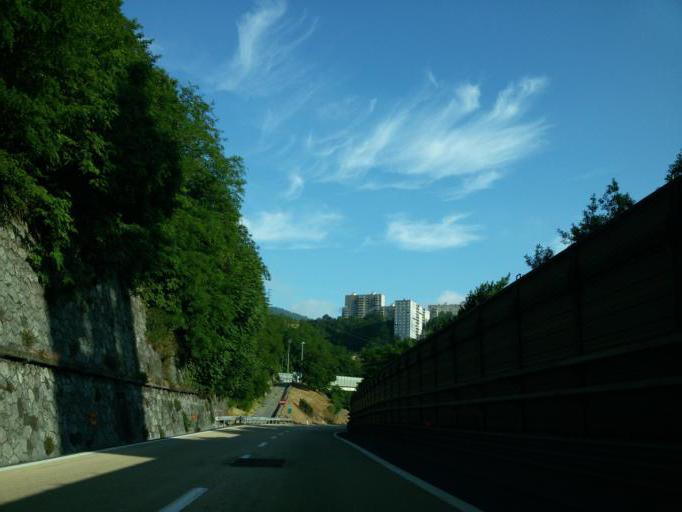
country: IT
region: Liguria
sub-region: Provincia di Genova
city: Manesseno
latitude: 44.4595
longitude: 8.9033
